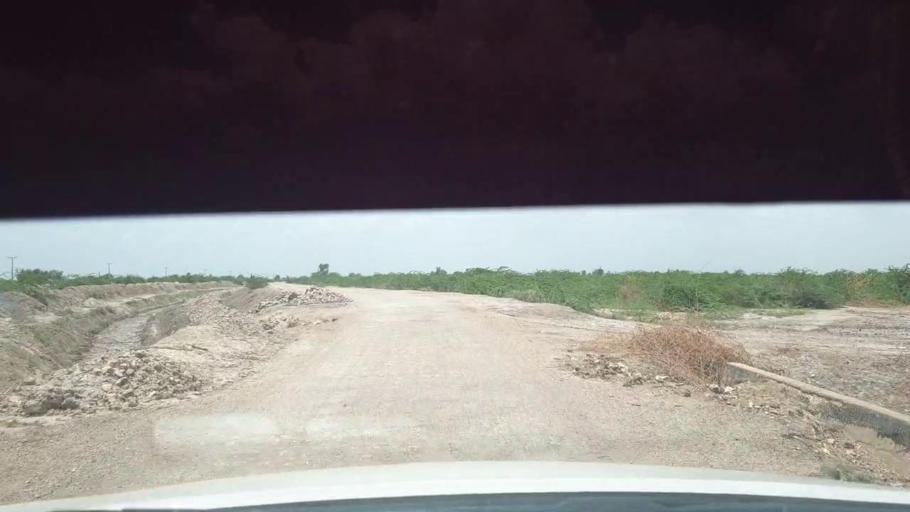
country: PK
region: Sindh
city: Kadhan
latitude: 24.5320
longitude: 69.1281
